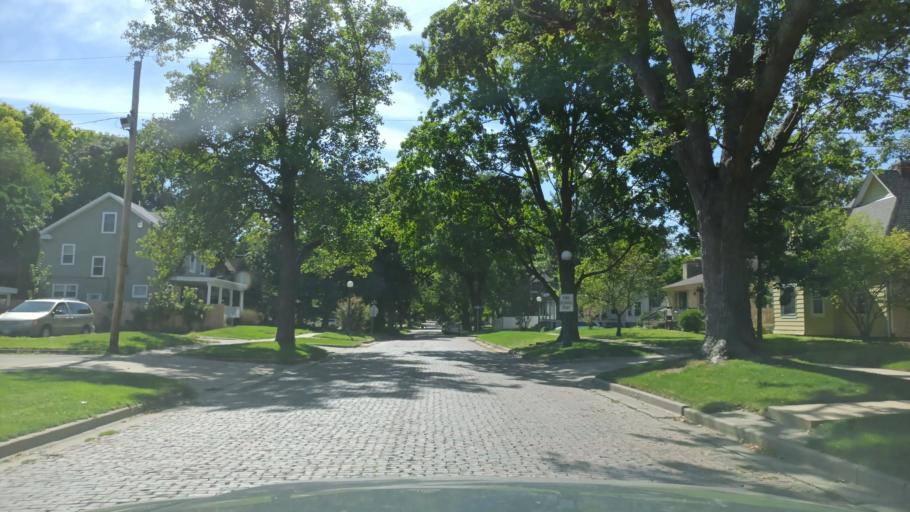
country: US
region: Illinois
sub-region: Champaign County
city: Champaign
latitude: 40.1142
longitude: -88.2501
